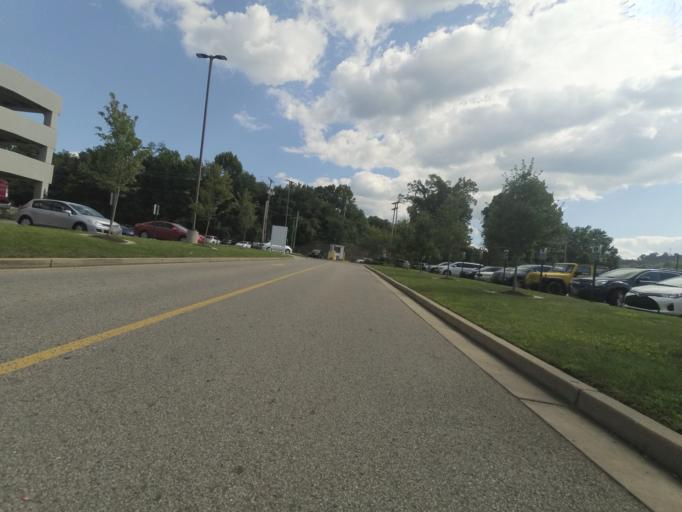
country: US
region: West Virginia
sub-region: Cabell County
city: Huntington
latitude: 38.4084
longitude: -82.4266
